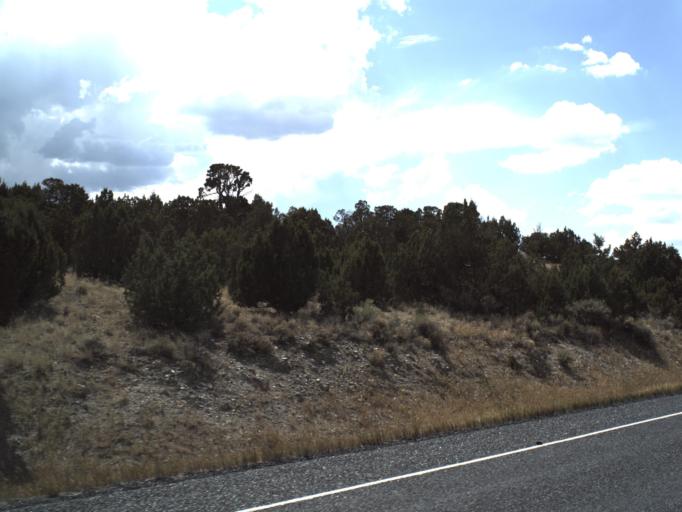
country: US
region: Idaho
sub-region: Minidoka County
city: Rupert
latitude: 41.9764
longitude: -113.1606
